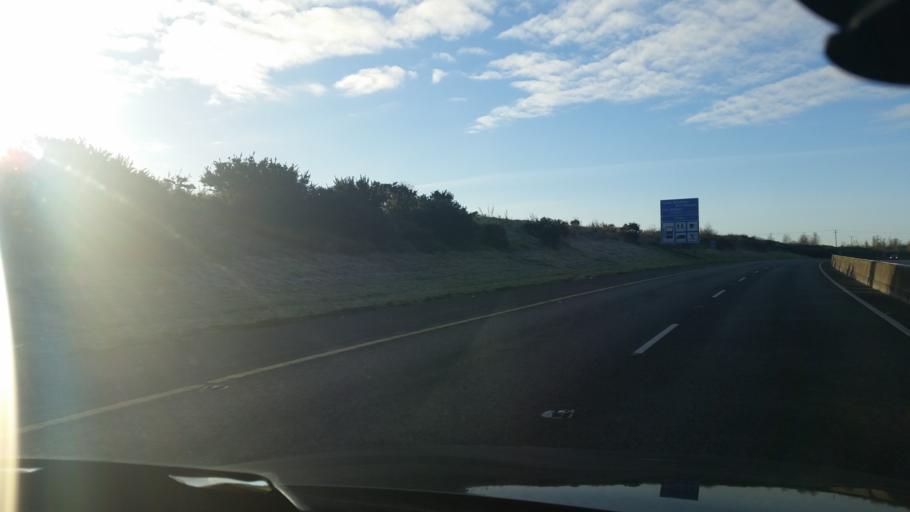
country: IE
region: Leinster
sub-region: Loch Garman
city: Castletown
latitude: 52.7543
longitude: -6.1948
